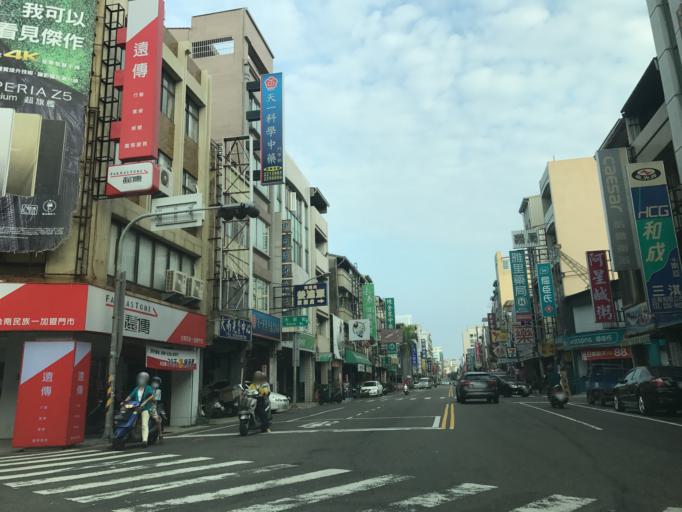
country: TW
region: Taiwan
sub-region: Tainan
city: Tainan
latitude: 23.0002
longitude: 120.1920
